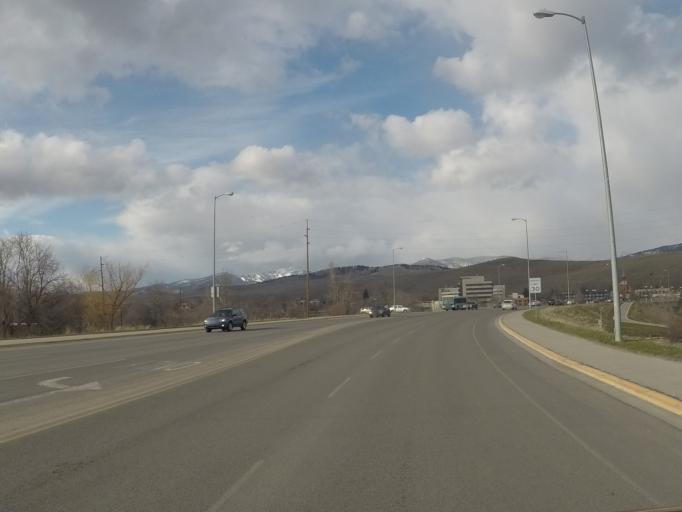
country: US
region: Montana
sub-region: Missoula County
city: Missoula
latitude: 46.8694
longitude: -114.0033
